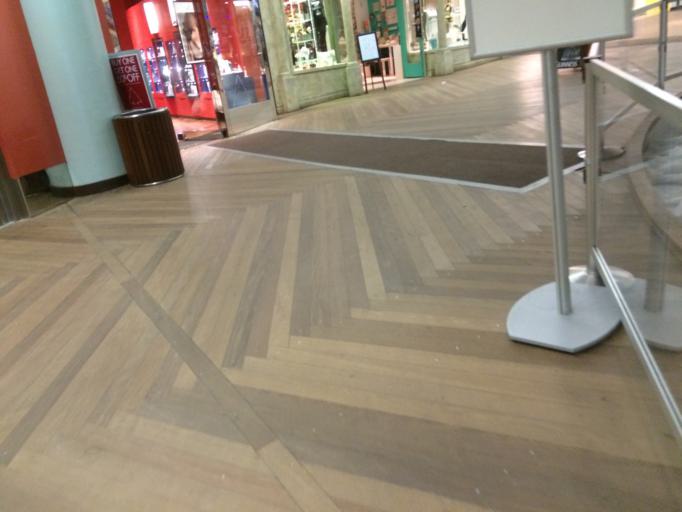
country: US
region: New Jersey
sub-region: Atlantic County
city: Atlantic City
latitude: 39.3550
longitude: -74.4353
